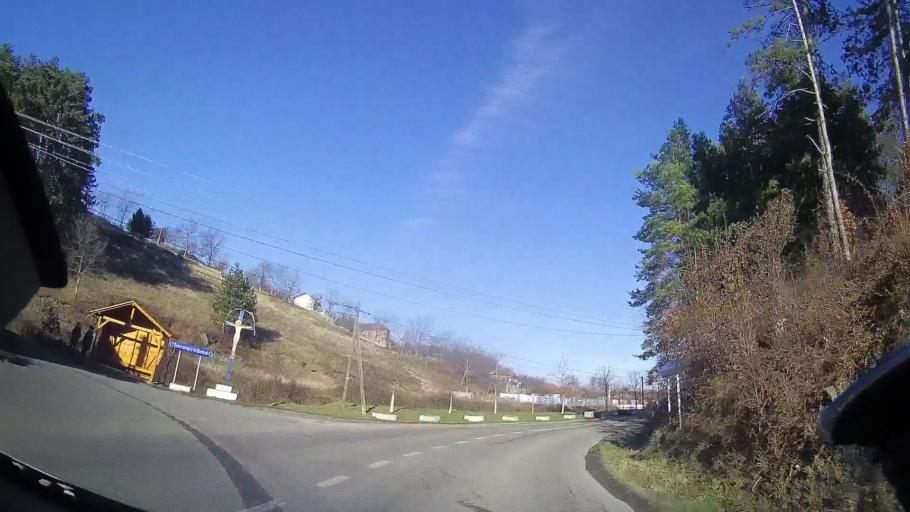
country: RO
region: Bihor
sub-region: Comuna Bratca
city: Bratca
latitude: 46.9305
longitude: 22.6009
